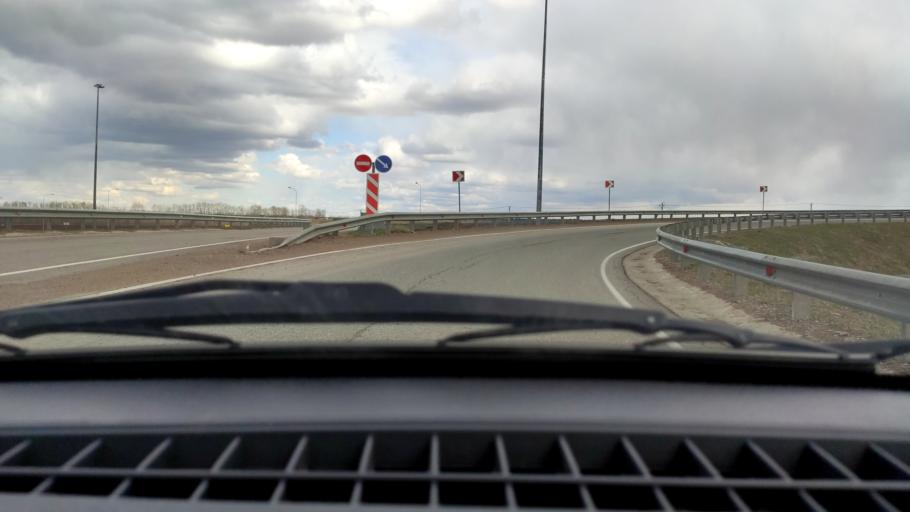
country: RU
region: Bashkortostan
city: Kushnarenkovo
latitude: 55.0800
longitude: 55.2773
